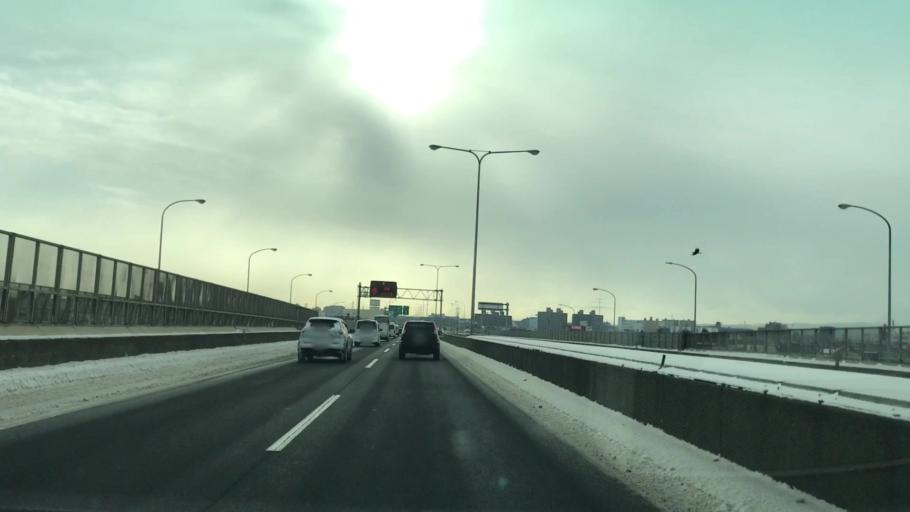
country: JP
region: Hokkaido
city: Sapporo
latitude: 43.0460
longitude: 141.4347
